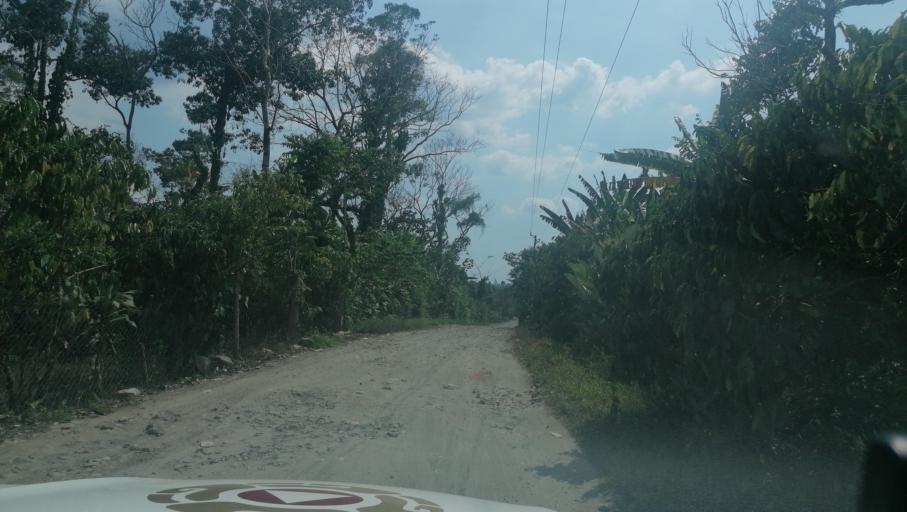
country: MX
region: Chiapas
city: Veinte de Noviembre
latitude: 15.0229
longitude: -92.2388
